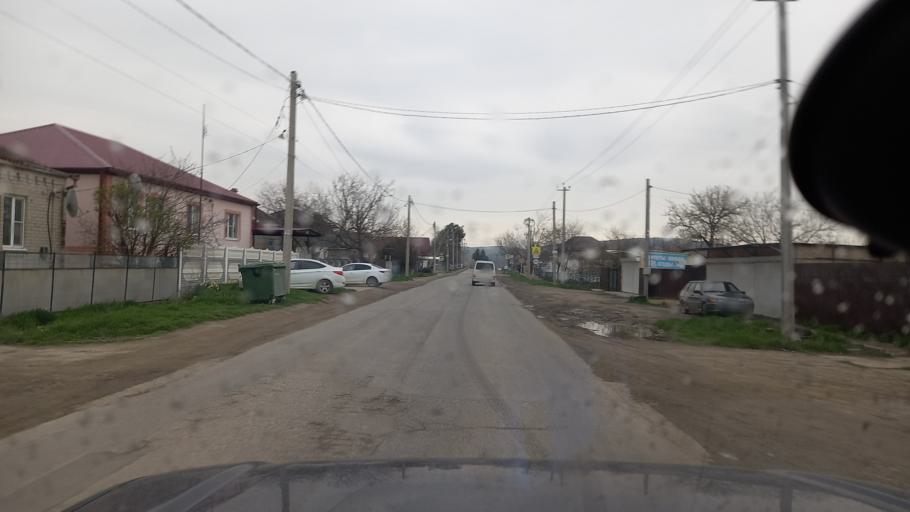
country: RU
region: Krasnodarskiy
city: Anapskaya
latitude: 44.8959
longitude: 37.4595
